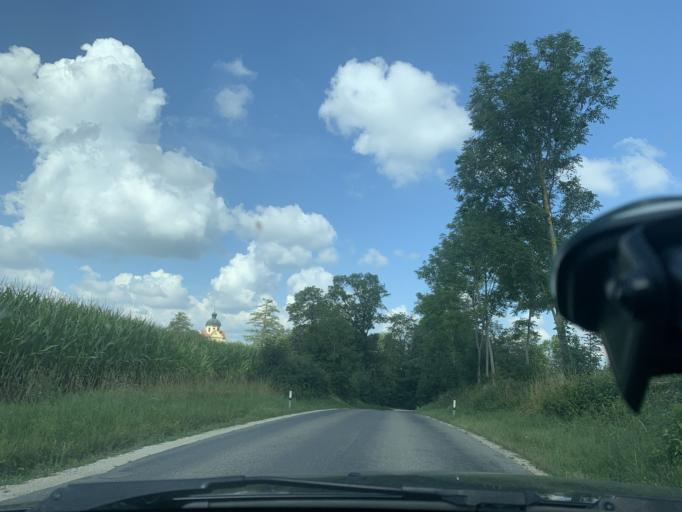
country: DE
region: Bavaria
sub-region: Swabia
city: Kissing
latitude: 48.2938
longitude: 10.9922
